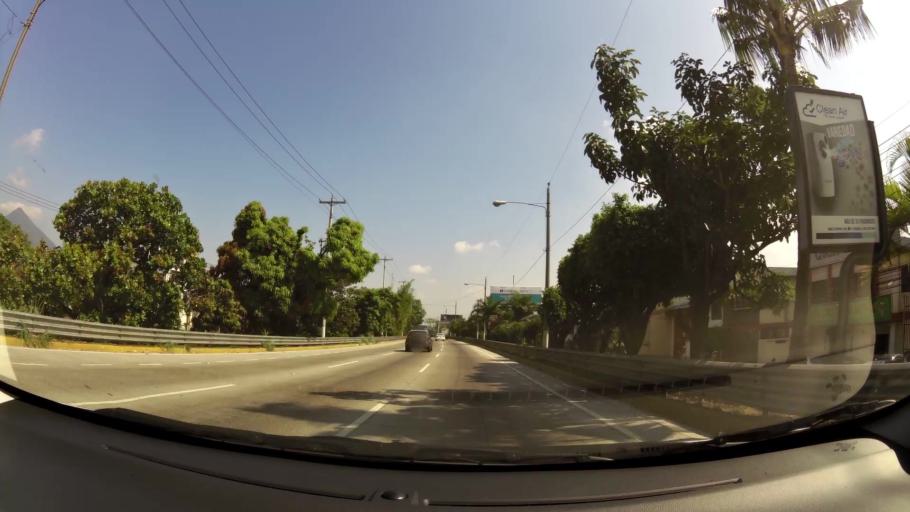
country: SV
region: La Libertad
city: Antiguo Cuscatlan
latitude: 13.6723
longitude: -89.2590
